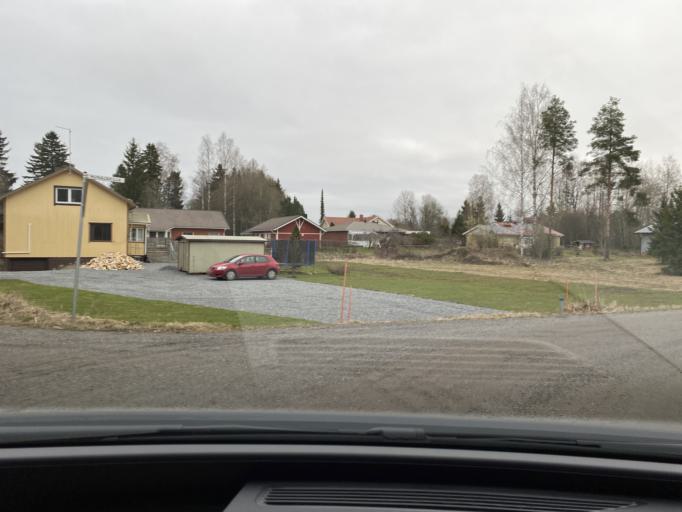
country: FI
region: Satakunta
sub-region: Pori
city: Huittinen
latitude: 61.1927
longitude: 22.7026
